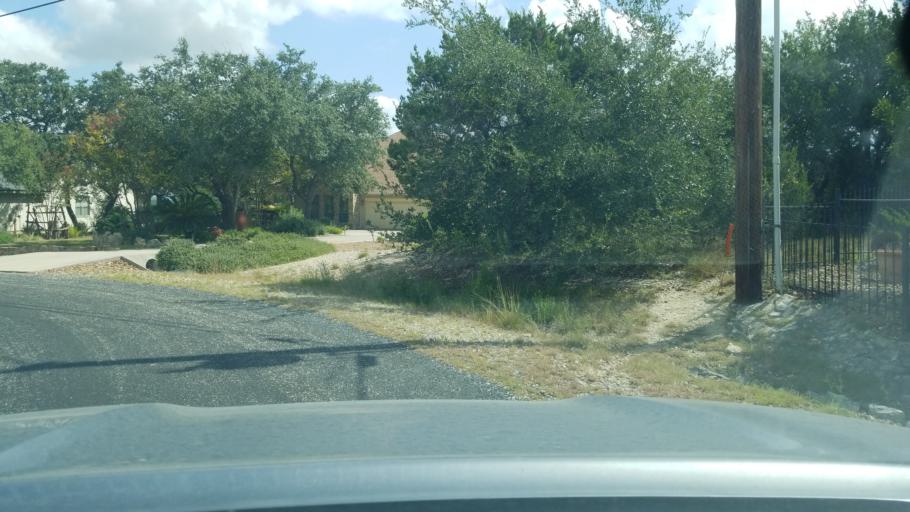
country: US
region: Texas
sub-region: Bexar County
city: Timberwood Park
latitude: 29.6884
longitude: -98.5127
